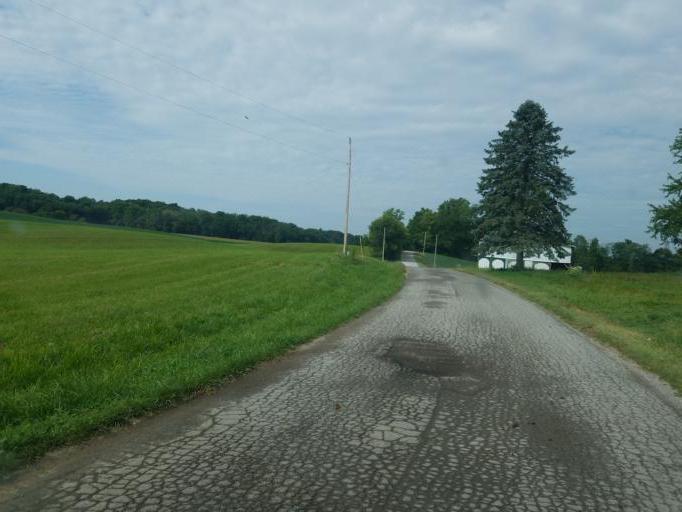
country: US
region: Ohio
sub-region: Knox County
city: Fredericktown
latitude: 40.4565
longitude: -82.6596
